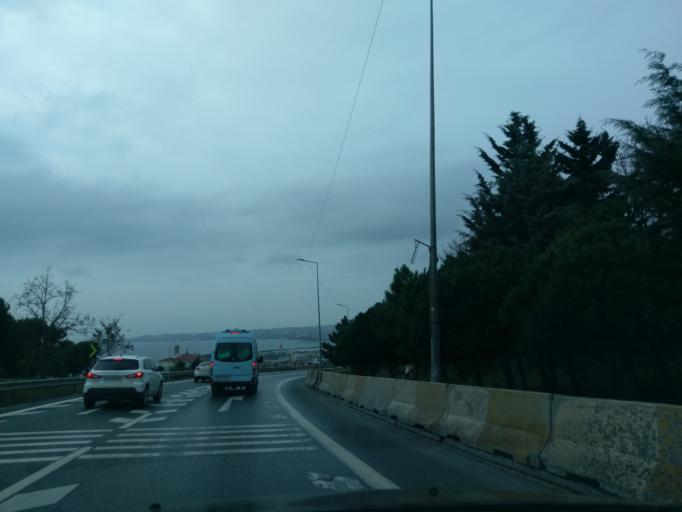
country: TR
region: Istanbul
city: Bueyuekcekmece
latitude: 41.0243
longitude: 28.5983
